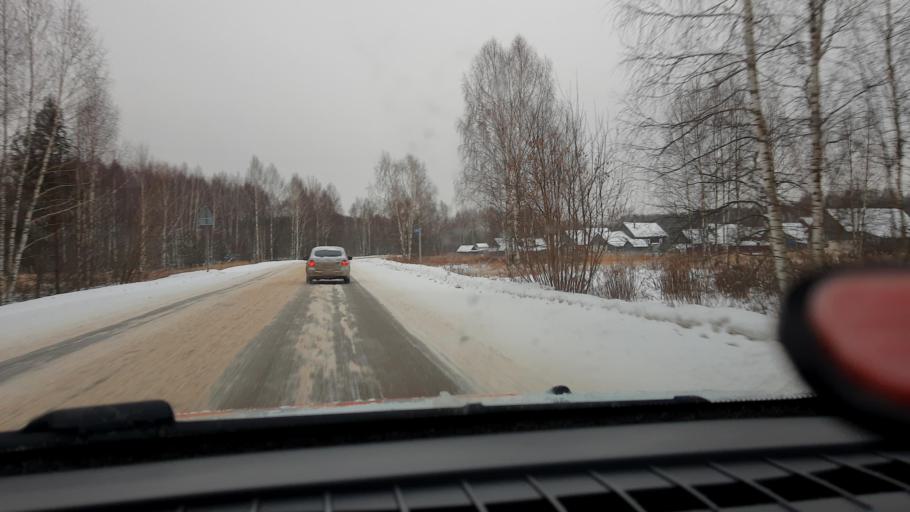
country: RU
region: Nizjnij Novgorod
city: Pamyat' Parizhskoy Kommuny
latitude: 56.2459
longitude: 44.4930
